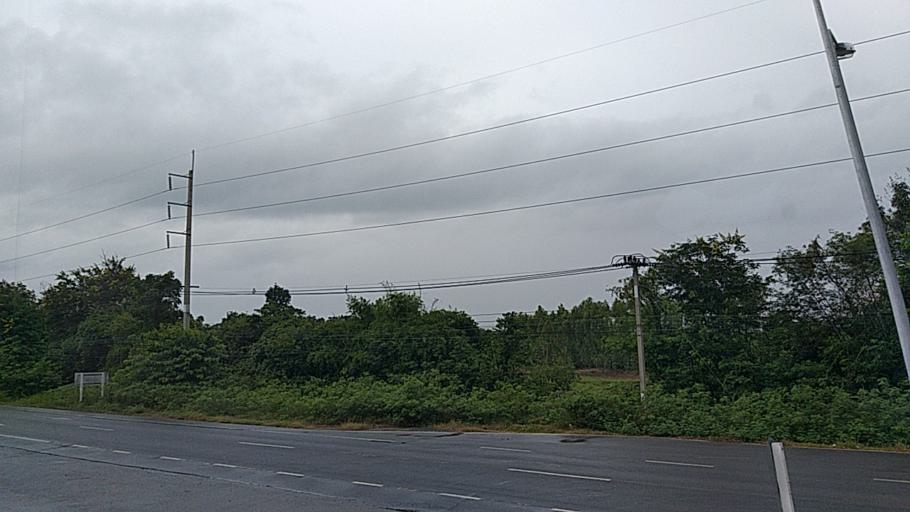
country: TH
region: Maha Sarakham
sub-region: Amphoe Borabue
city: Borabue
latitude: 16.0731
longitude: 103.1517
